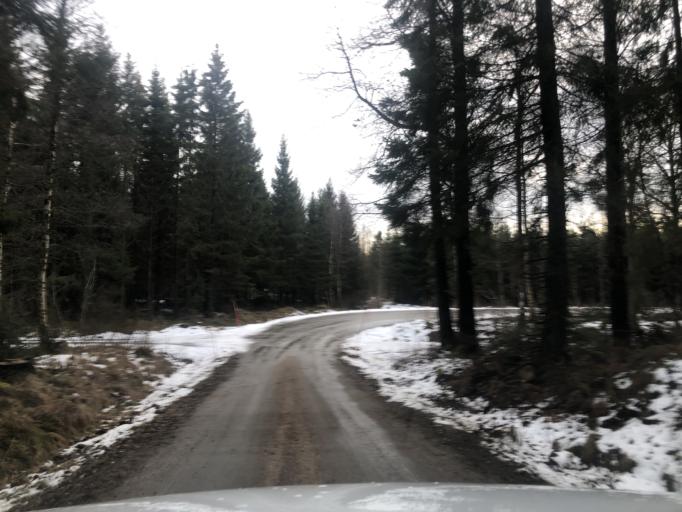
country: SE
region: Vaestra Goetaland
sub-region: Ulricehamns Kommun
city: Ulricehamn
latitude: 57.7772
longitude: 13.4769
